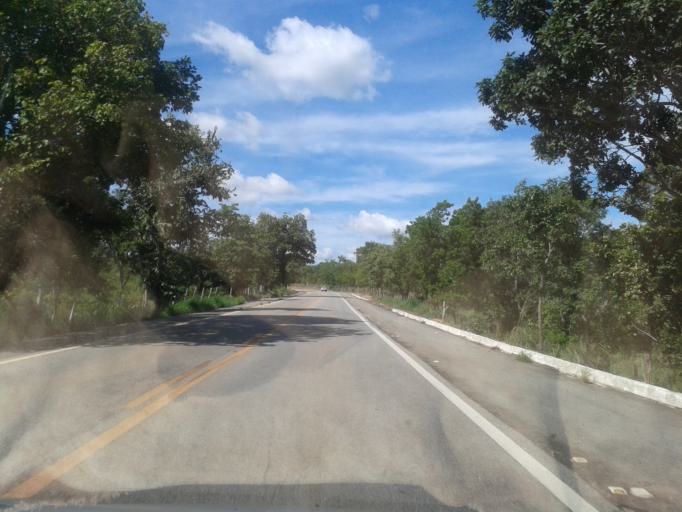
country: BR
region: Goias
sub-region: Itapuranga
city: Itapuranga
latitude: -15.3771
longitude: -50.3879
